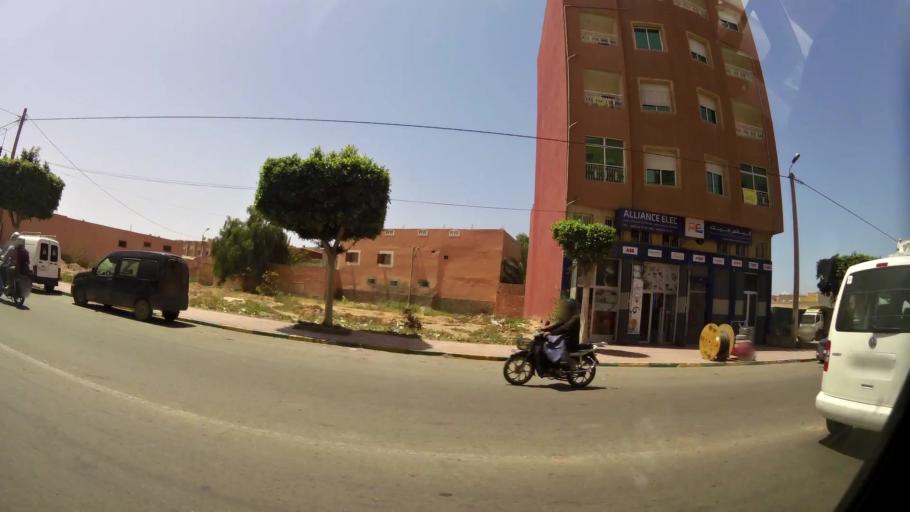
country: MA
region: Souss-Massa-Draa
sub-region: Inezgane-Ait Mellou
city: Inezgane
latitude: 30.3408
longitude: -9.4966
